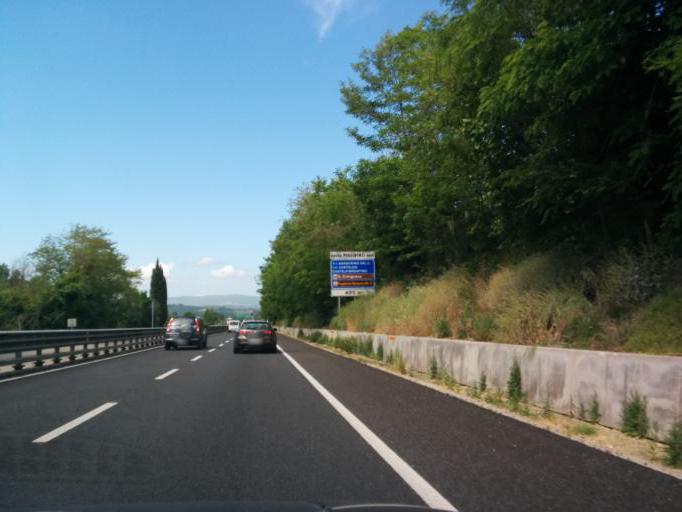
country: IT
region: Tuscany
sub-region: Provincia di Siena
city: Poggibonsi
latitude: 43.4874
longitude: 11.1603
